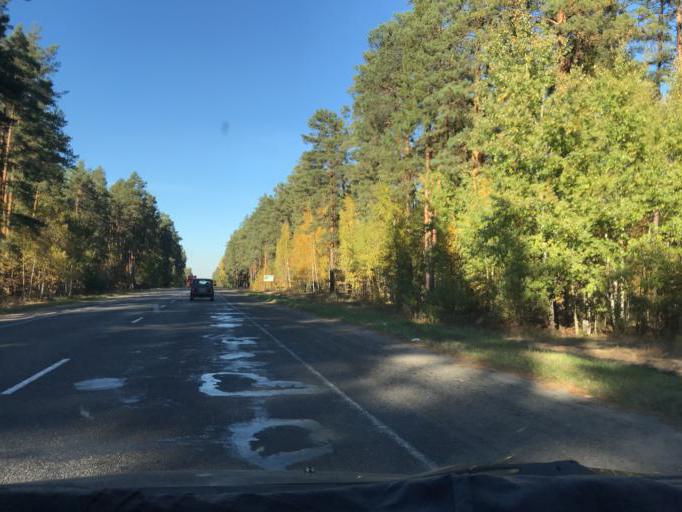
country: BY
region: Gomel
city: Kalinkavichy
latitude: 52.0594
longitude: 29.3611
